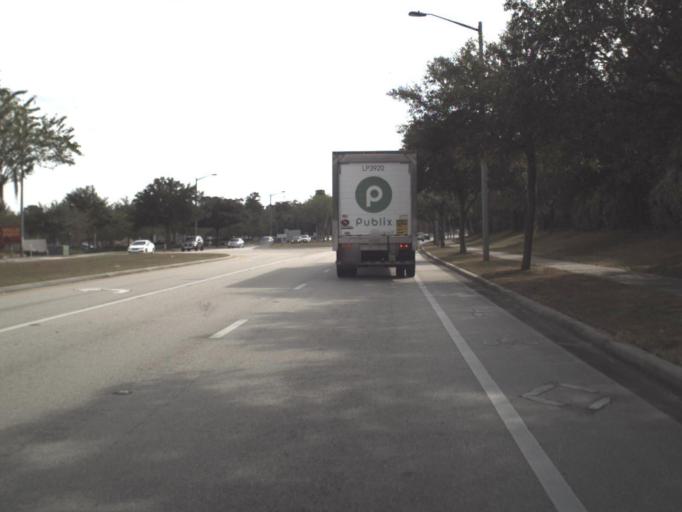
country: US
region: Florida
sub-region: Orange County
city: Taft
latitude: 28.4129
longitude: -81.2431
